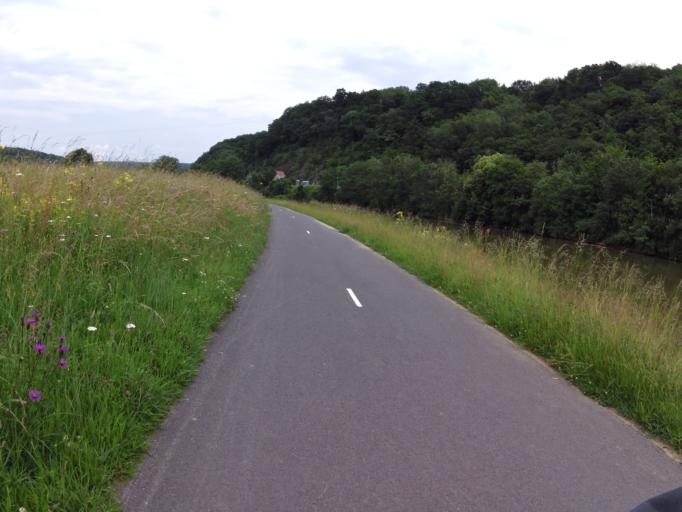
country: FR
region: Champagne-Ardenne
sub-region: Departement des Ardennes
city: Montcy-Notre-Dame
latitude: 49.7728
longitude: 4.7509
